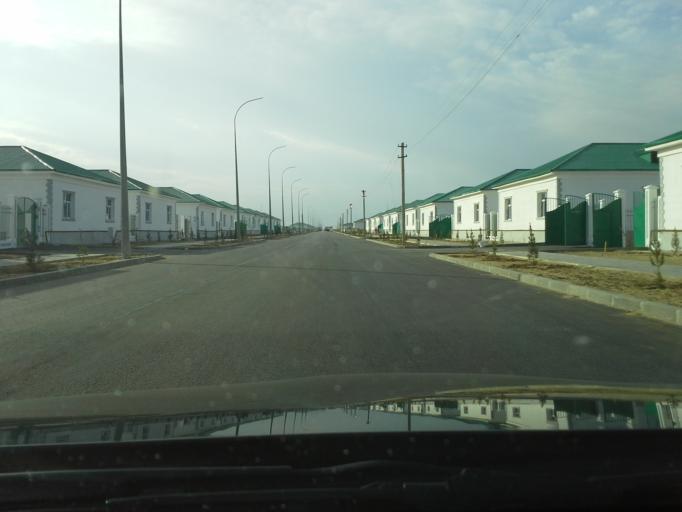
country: TM
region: Ahal
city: Abadan
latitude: 38.0969
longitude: 58.3153
